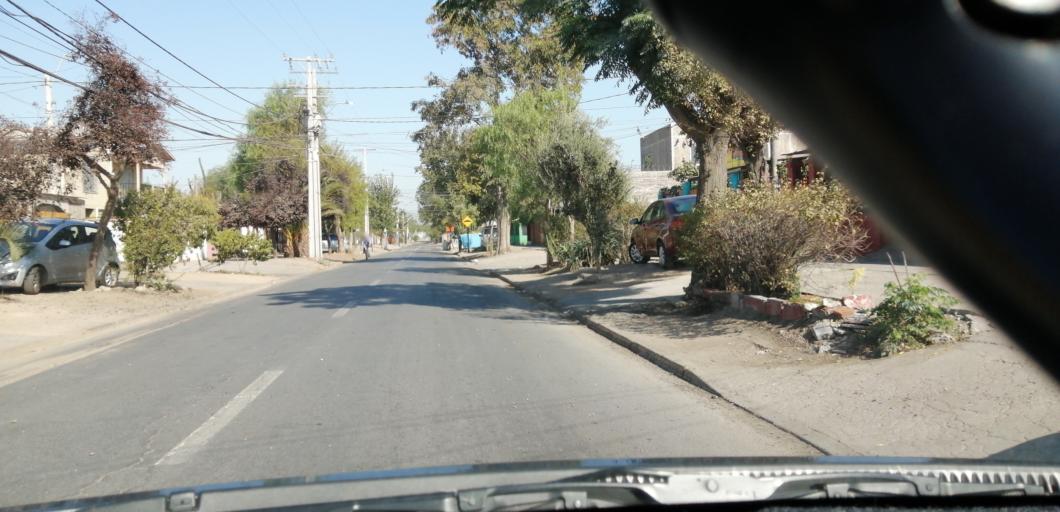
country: CL
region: Santiago Metropolitan
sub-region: Provincia de Santiago
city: Lo Prado
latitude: -33.4419
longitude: -70.7436
